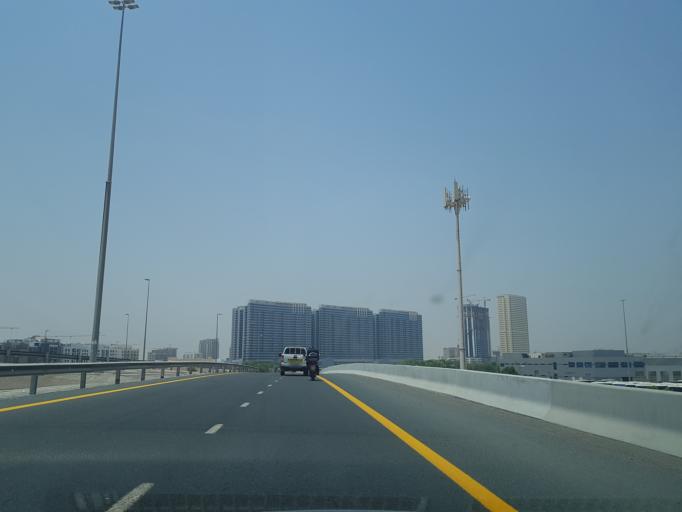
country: AE
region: Dubai
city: Dubai
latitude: 25.0897
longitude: 55.3937
